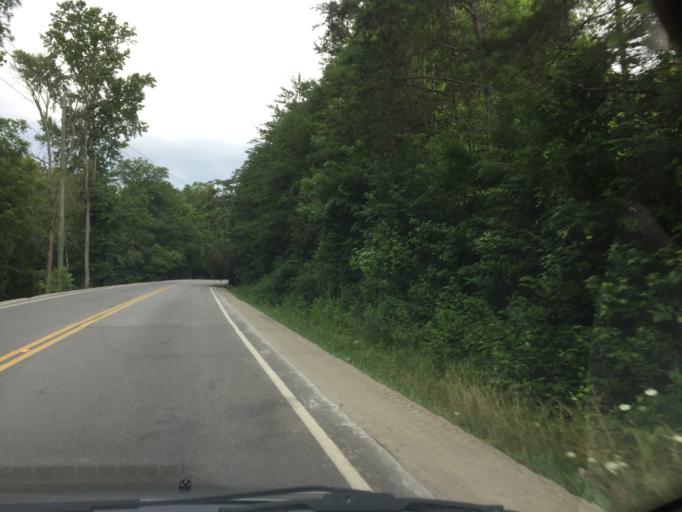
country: US
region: Tennessee
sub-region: Hamilton County
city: Apison
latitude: 34.9892
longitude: -85.0706
